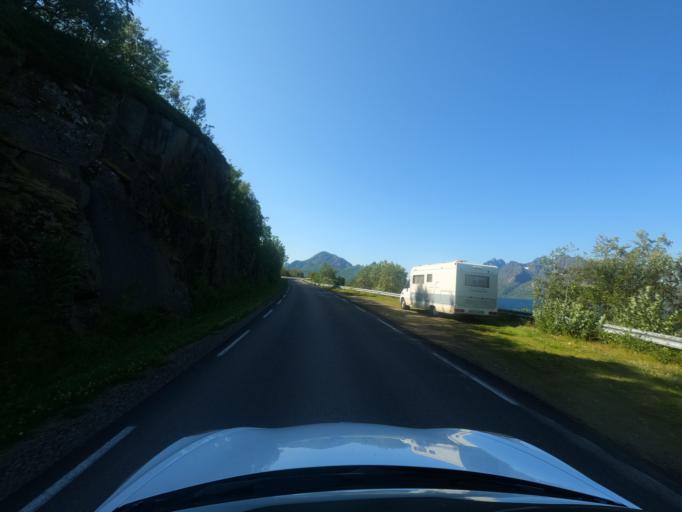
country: NO
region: Nordland
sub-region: Hadsel
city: Stokmarknes
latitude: 68.3265
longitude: 15.0097
